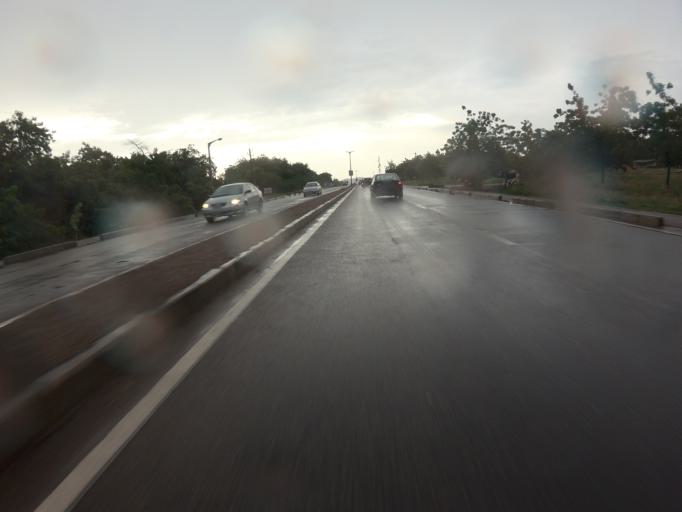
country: GH
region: Upper East
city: Bolgatanga
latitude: 10.7973
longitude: -0.8594
